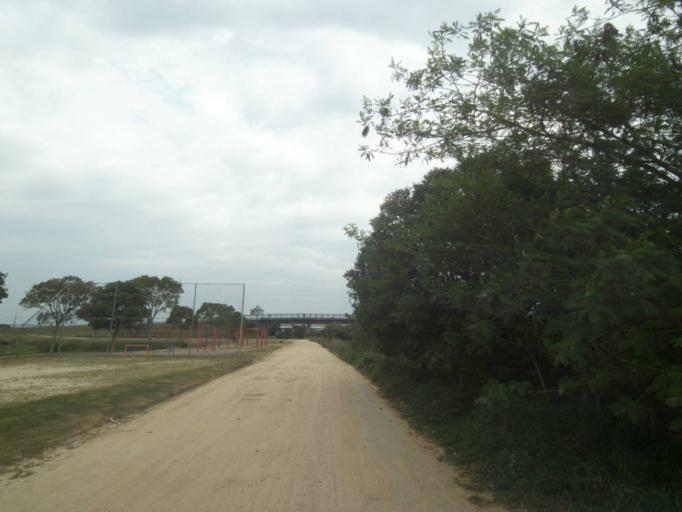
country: BR
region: Parana
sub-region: Sao Jose Dos Pinhais
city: Sao Jose dos Pinhais
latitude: -25.5001
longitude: -49.2067
